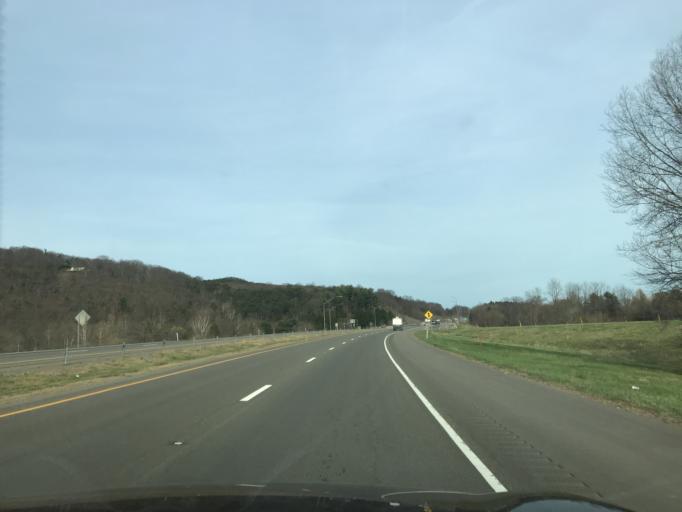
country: US
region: Pennsylvania
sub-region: Lycoming County
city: Montoursville
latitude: 41.2645
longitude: -76.9186
